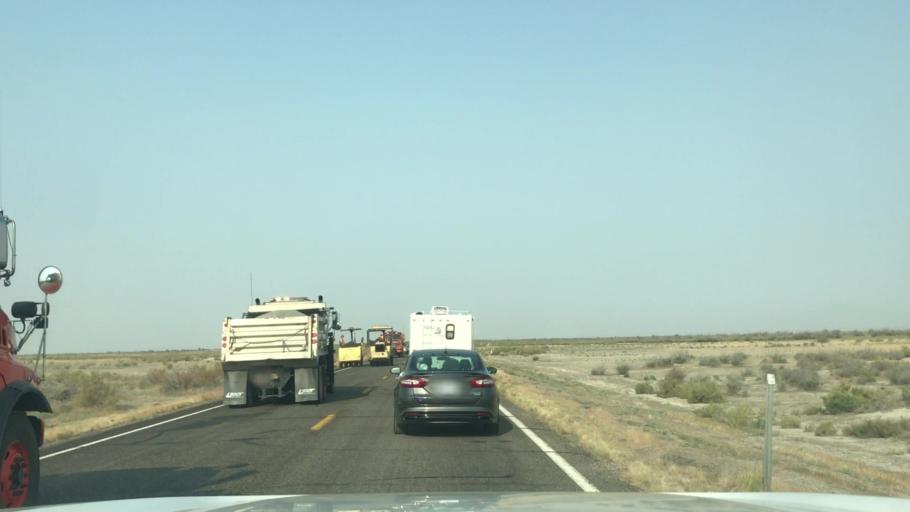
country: US
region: Utah
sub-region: Millard County
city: Delta
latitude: 39.3102
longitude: -112.7765
